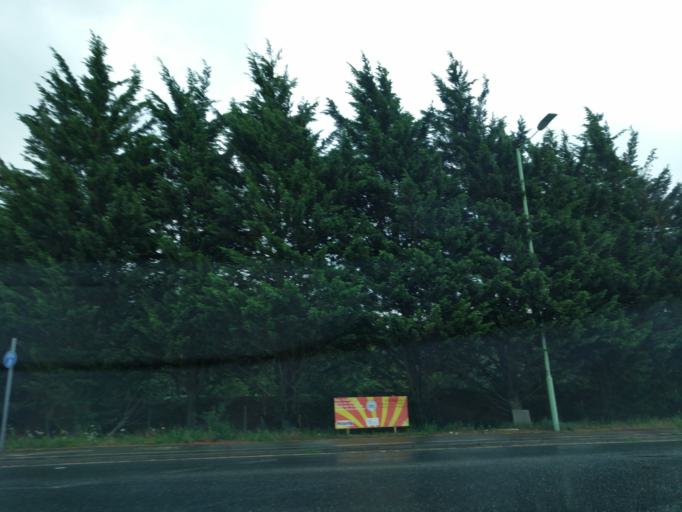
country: GB
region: England
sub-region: Suffolk
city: Lakenheath
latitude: 52.3612
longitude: 0.5139
